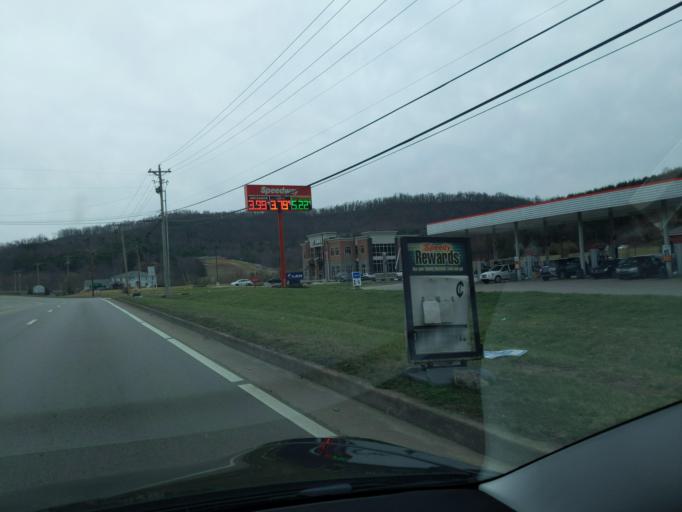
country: US
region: Kentucky
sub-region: Whitley County
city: Corbin
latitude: 36.9184
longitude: -84.1223
